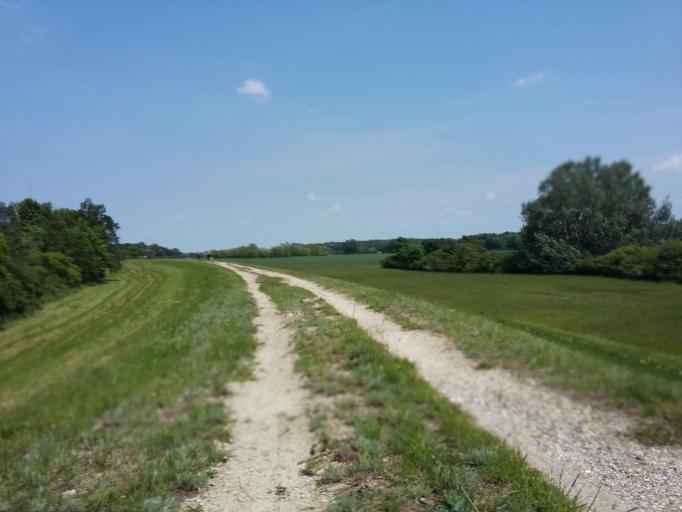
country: AT
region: Lower Austria
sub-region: Politischer Bezirk Ganserndorf
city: Angern an der March
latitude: 48.4172
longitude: 16.8642
